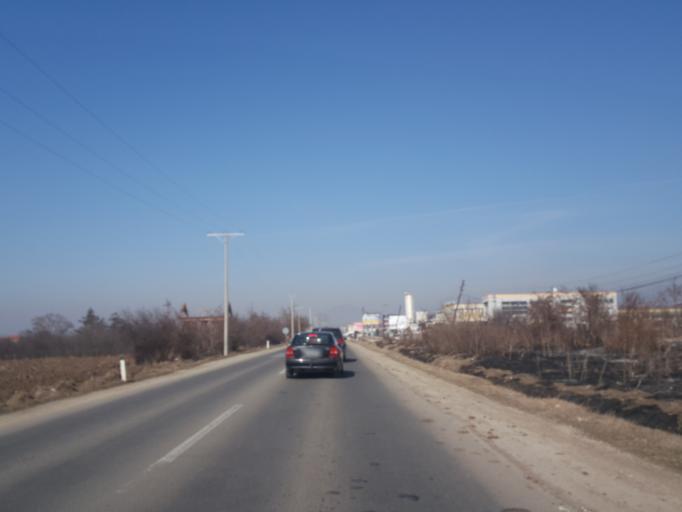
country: XK
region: Mitrovica
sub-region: Vushtrri
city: Vushtrri
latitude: 42.7974
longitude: 20.9982
